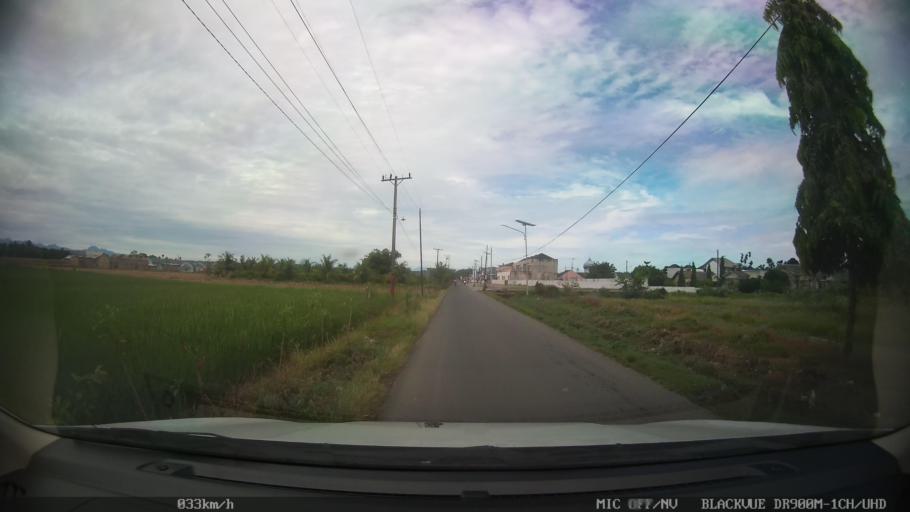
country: ID
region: North Sumatra
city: Sunggal
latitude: 3.5727
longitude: 98.5754
